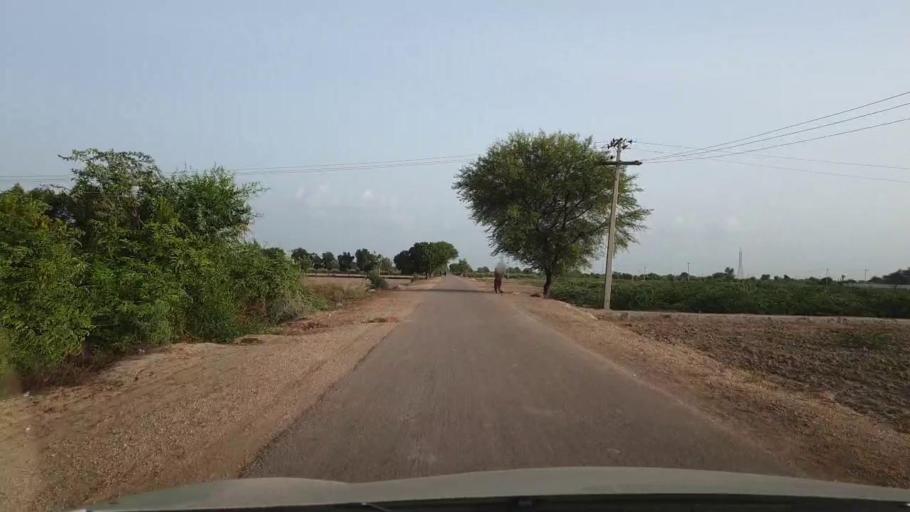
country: PK
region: Sindh
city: Tando Ghulam Ali
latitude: 25.1172
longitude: 68.8849
